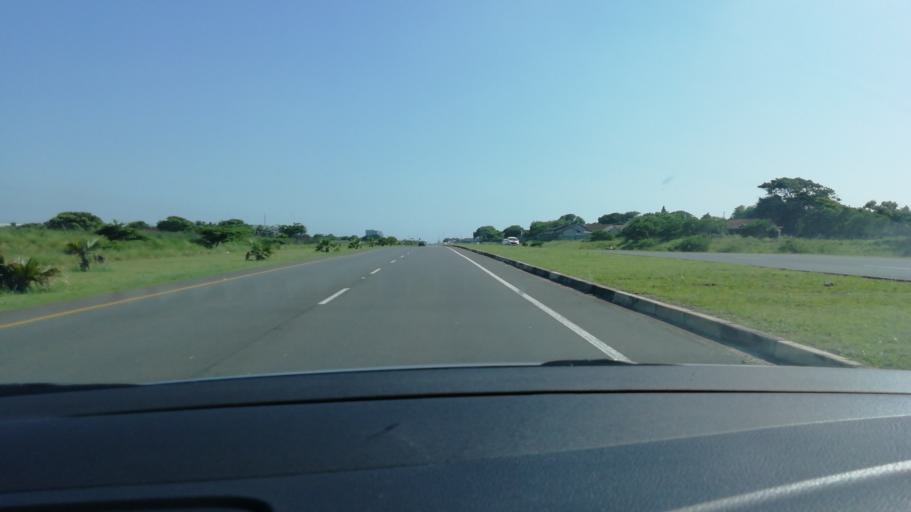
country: ZA
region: KwaZulu-Natal
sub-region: uThungulu District Municipality
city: Richards Bay
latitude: -28.7643
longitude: 32.0490
